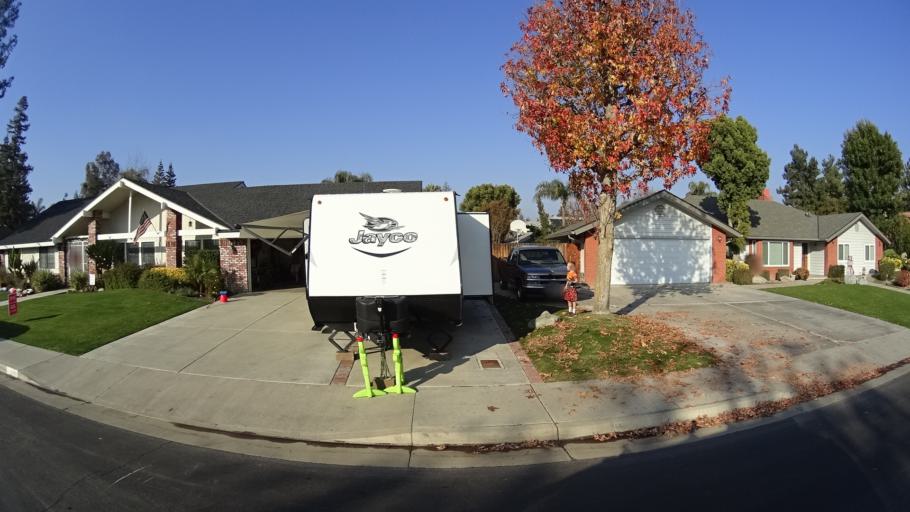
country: US
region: California
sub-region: Kern County
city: Greenacres
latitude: 35.3332
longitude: -119.1005
